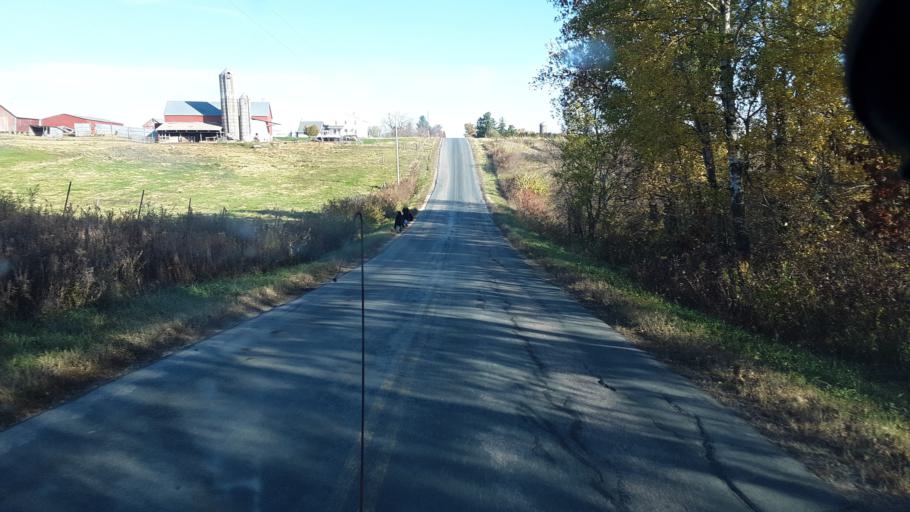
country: US
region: Wisconsin
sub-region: Vernon County
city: Hillsboro
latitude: 43.7935
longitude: -90.4432
